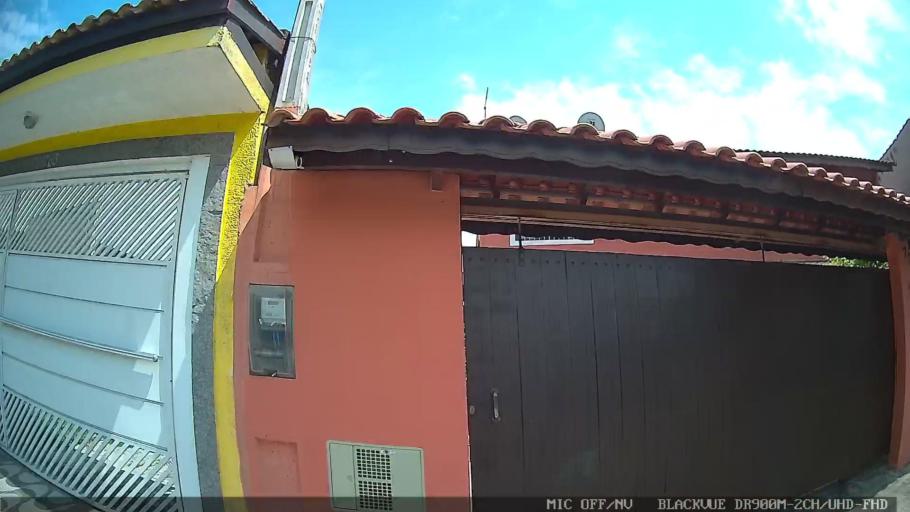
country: BR
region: Sao Paulo
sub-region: Caraguatatuba
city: Caraguatatuba
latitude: -23.6738
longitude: -45.4506
